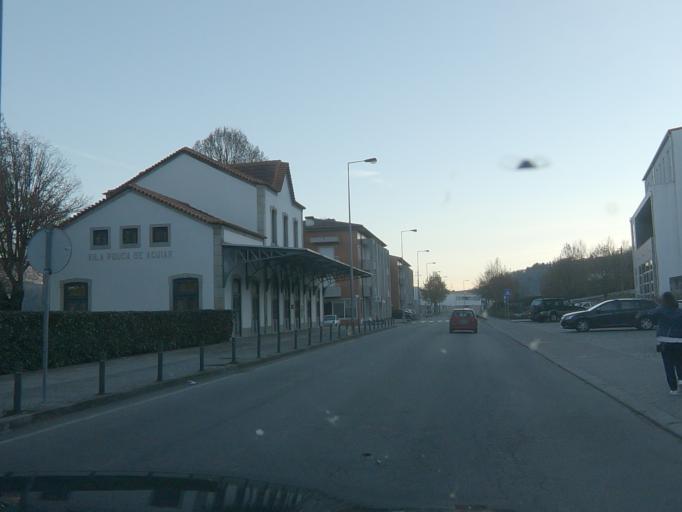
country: PT
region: Vila Real
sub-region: Vila Pouca de Aguiar
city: Vila Pouca de Aguiar
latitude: 41.5004
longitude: -7.6466
